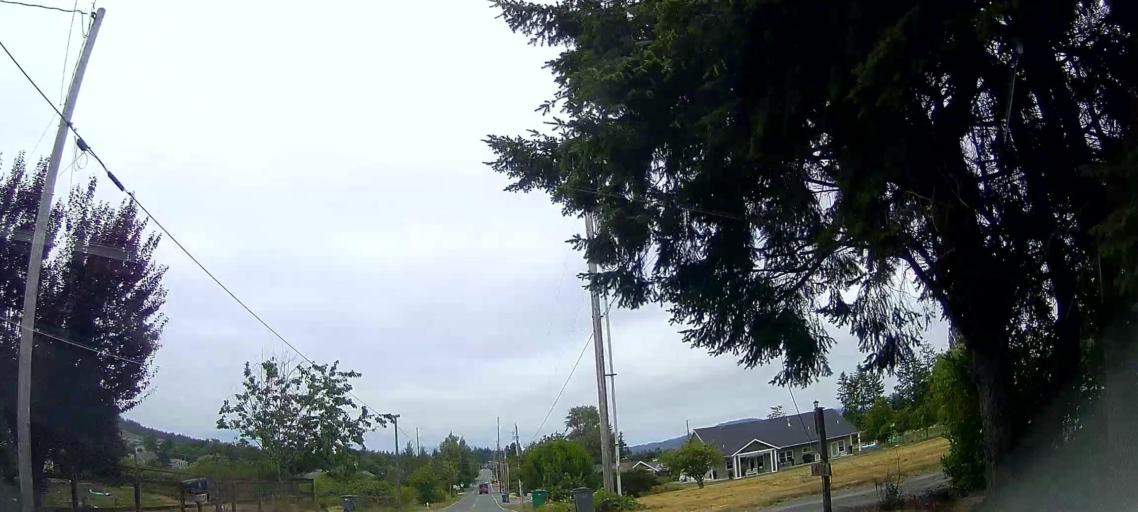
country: US
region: Washington
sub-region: Skagit County
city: Anacortes
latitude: 48.4862
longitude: -122.6251
